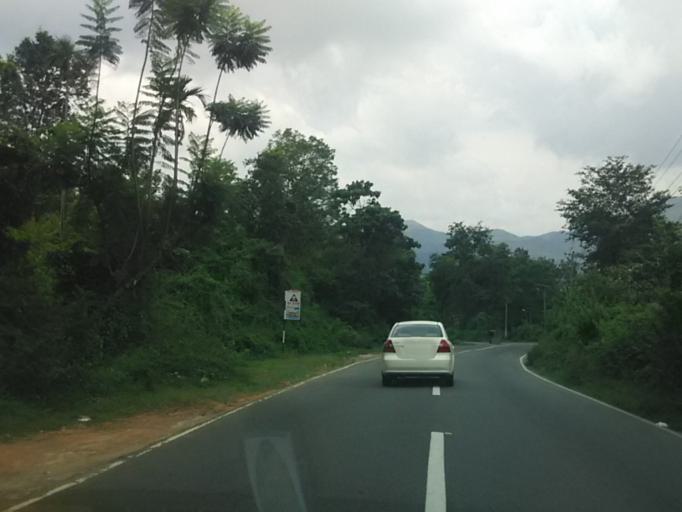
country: IN
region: Kerala
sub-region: Wayanad
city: Kalpetta
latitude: 11.5925
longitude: 76.0715
